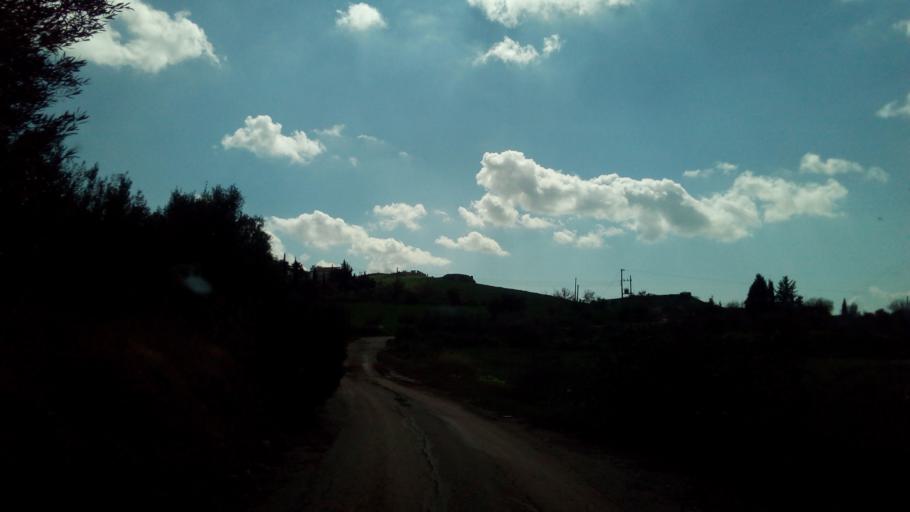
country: CY
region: Pafos
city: Mesogi
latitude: 34.7725
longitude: 32.5837
